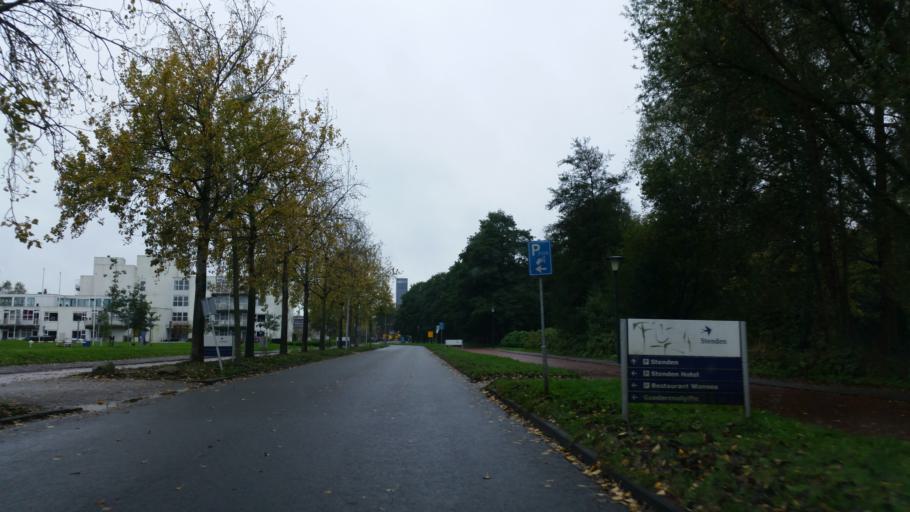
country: NL
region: Friesland
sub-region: Gemeente Leeuwarden
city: Bilgaard
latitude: 53.2101
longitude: 5.7953
